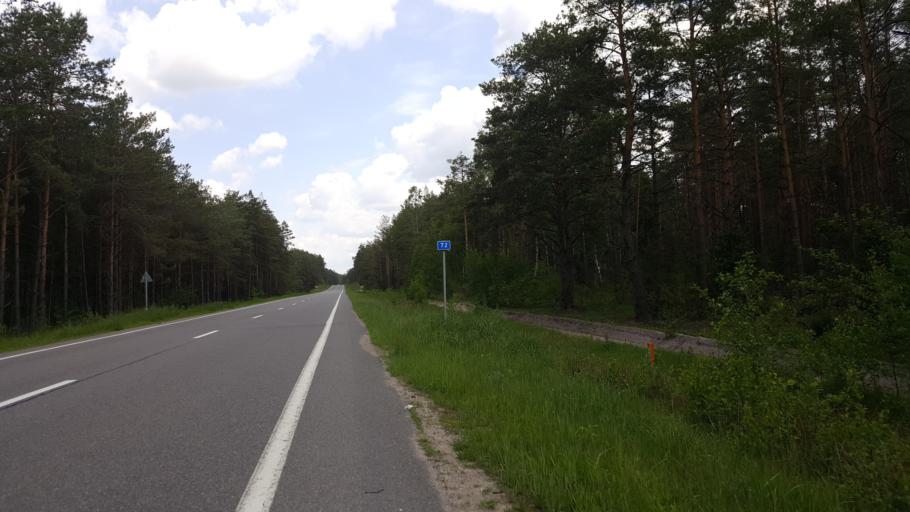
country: BY
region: Brest
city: Zhabinka
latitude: 52.4284
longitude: 24.1246
